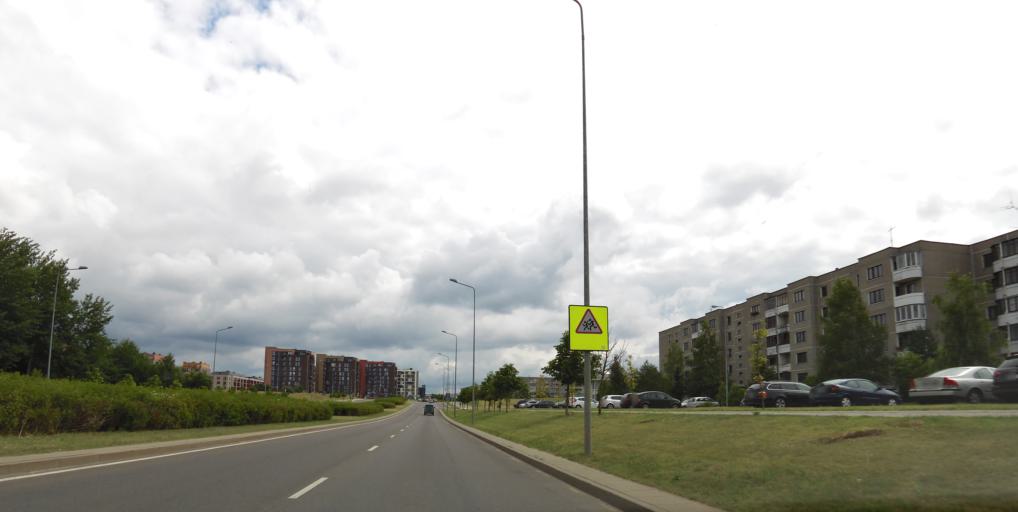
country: LT
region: Vilnius County
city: Pilaite
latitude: 54.7102
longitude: 25.1775
